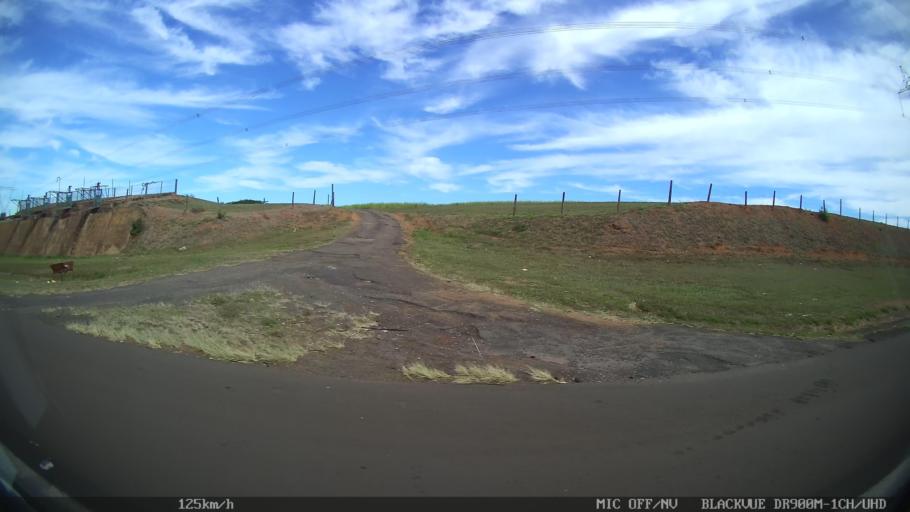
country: BR
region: Sao Paulo
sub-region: Matao
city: Matao
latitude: -21.5512
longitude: -48.4892
